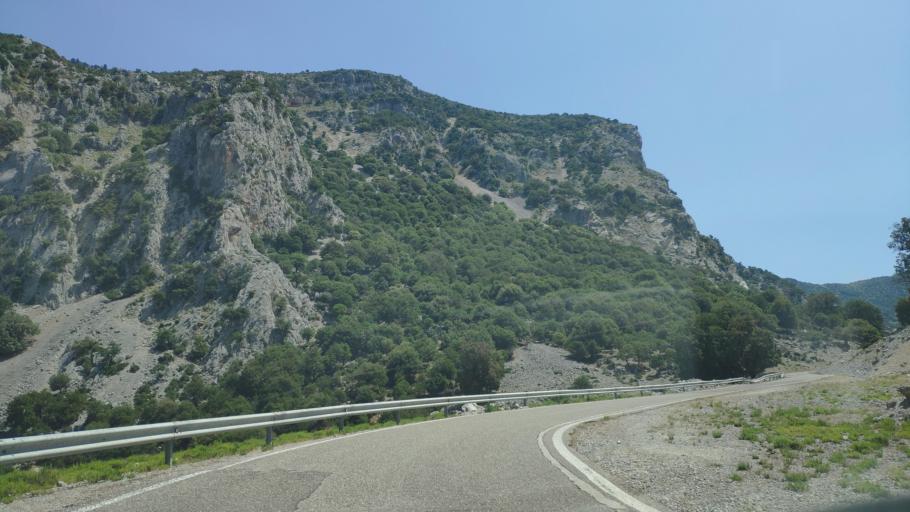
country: GR
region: West Greece
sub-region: Nomos Aitolias kai Akarnanias
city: Krikellos
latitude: 39.0201
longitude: 21.3368
